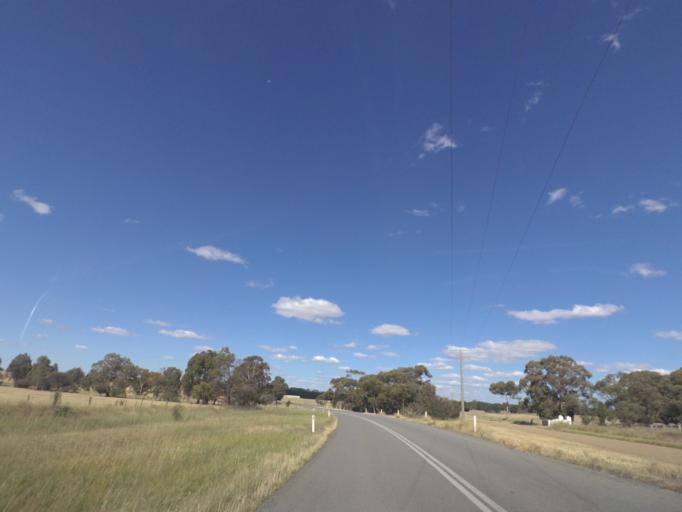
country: AU
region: Victoria
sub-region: Hume
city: Sunbury
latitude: -37.4398
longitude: 144.8329
